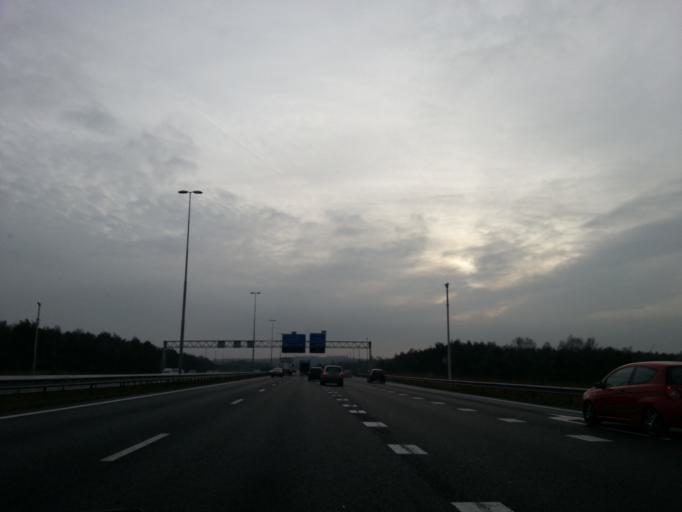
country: NL
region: Gelderland
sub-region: Gemeente Rozendaal
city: Rozendaal
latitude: 52.0294
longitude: 5.9266
